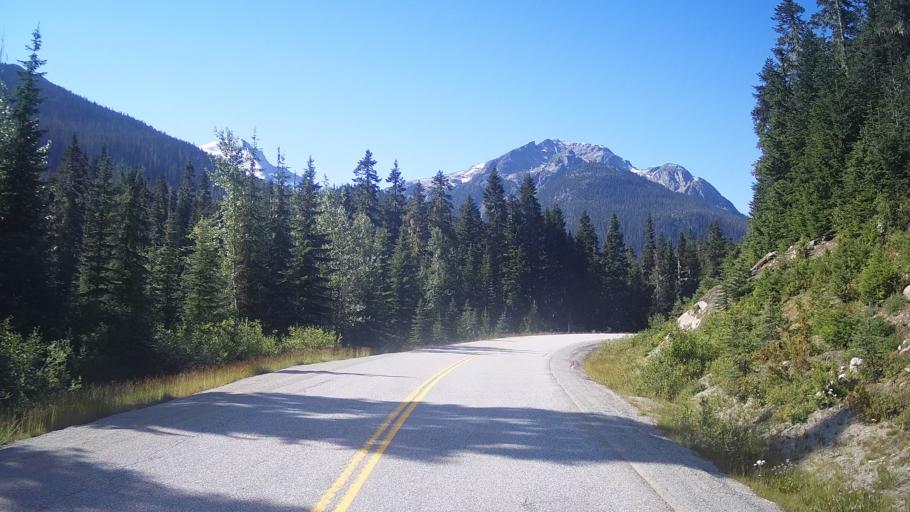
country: CA
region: British Columbia
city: Pemberton
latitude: 50.3784
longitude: -122.4869
